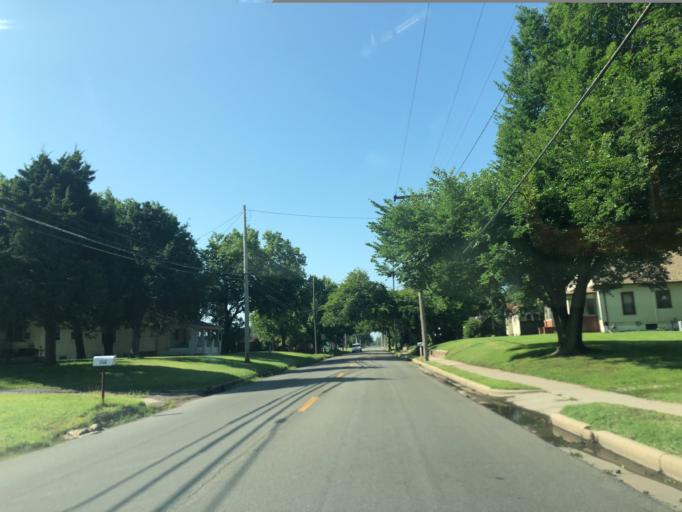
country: US
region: Kansas
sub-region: Sedgwick County
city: Wichita
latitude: 37.7473
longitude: -97.3449
